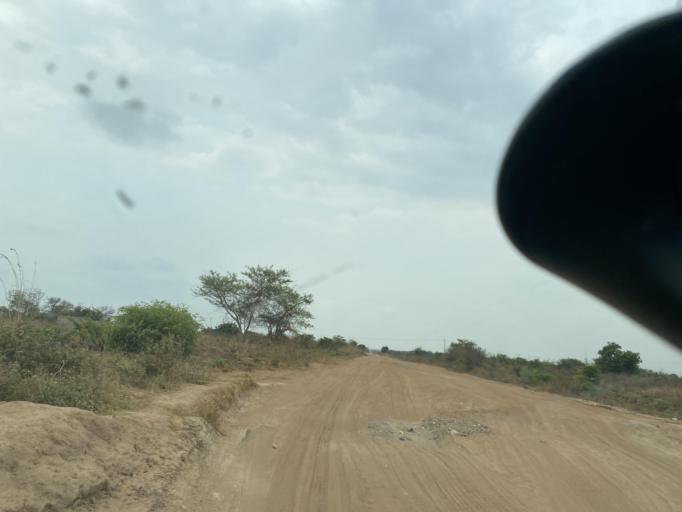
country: ZM
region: Lusaka
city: Lusaka
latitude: -15.2185
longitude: 28.3378
